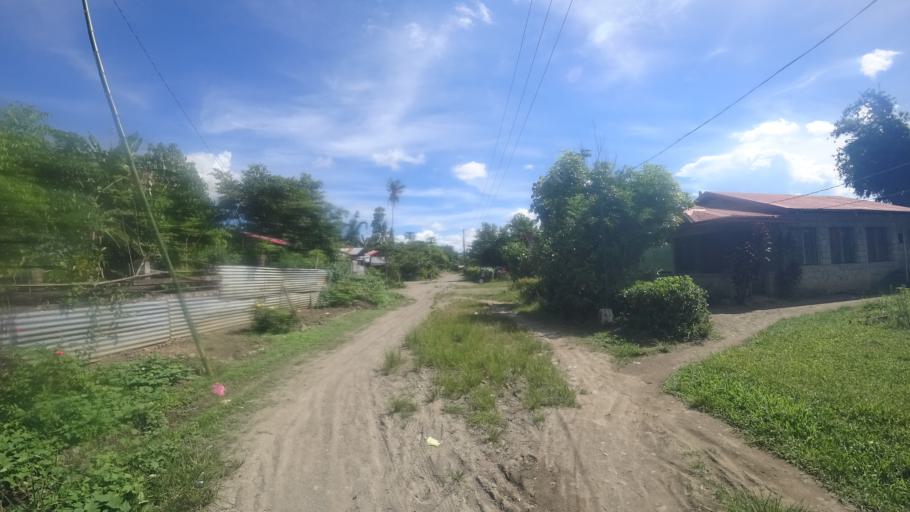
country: PH
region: Eastern Visayas
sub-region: Province of Leyte
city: Pastrana
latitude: 11.1544
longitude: 124.8582
